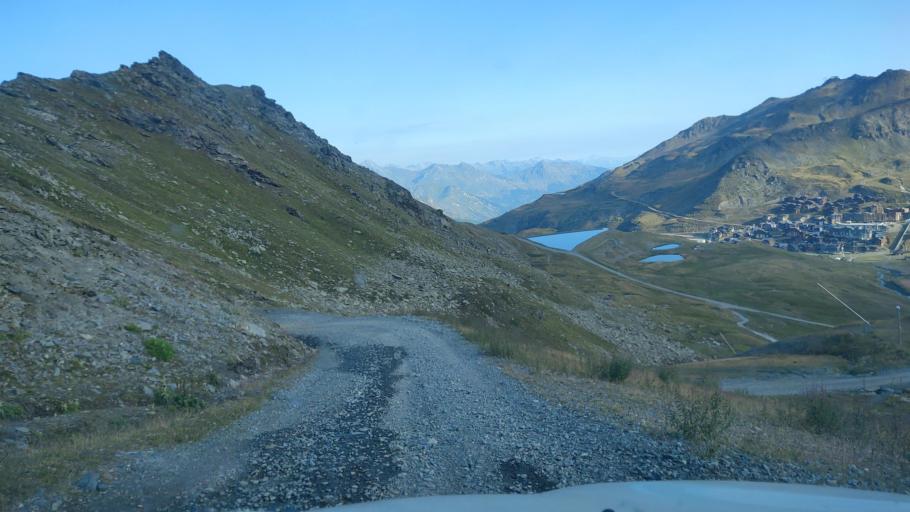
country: FR
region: Rhone-Alpes
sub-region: Departement de la Savoie
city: Val Thorens
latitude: 45.2782
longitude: 6.5817
